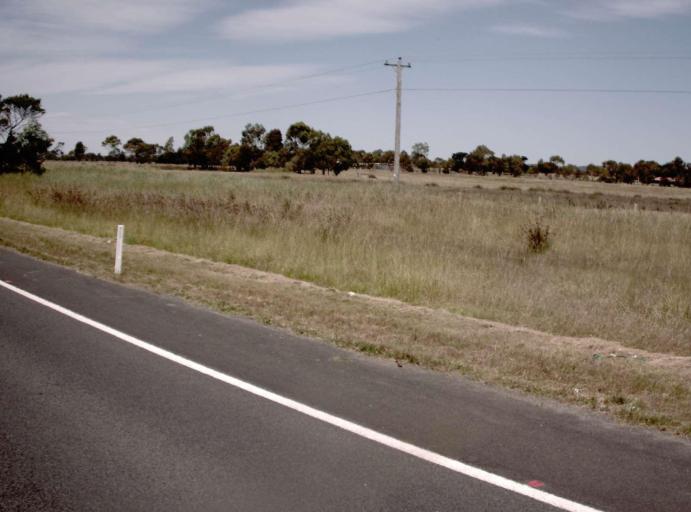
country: AU
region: Victoria
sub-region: Wellington
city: Heyfield
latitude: -38.1570
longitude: 146.7492
